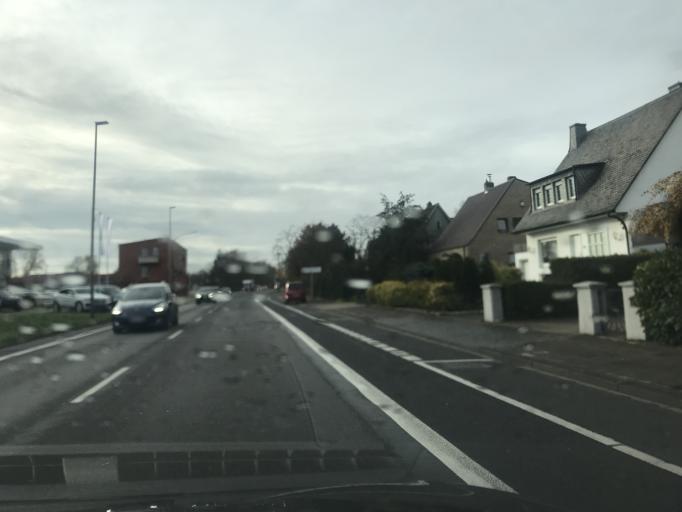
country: DE
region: North Rhine-Westphalia
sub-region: Regierungsbezirk Arnsberg
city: Hamm
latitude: 51.6780
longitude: 7.8518
